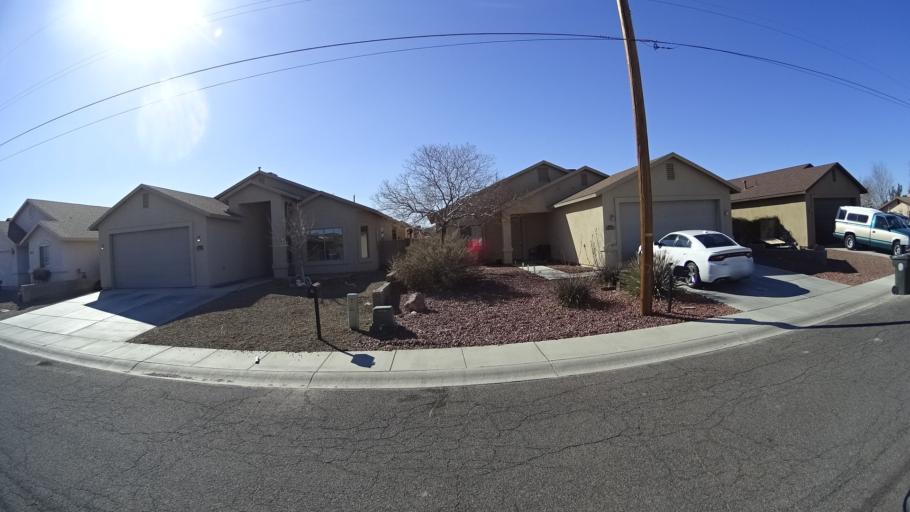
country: US
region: Arizona
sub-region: Mohave County
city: Kingman
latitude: 35.1986
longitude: -114.0176
